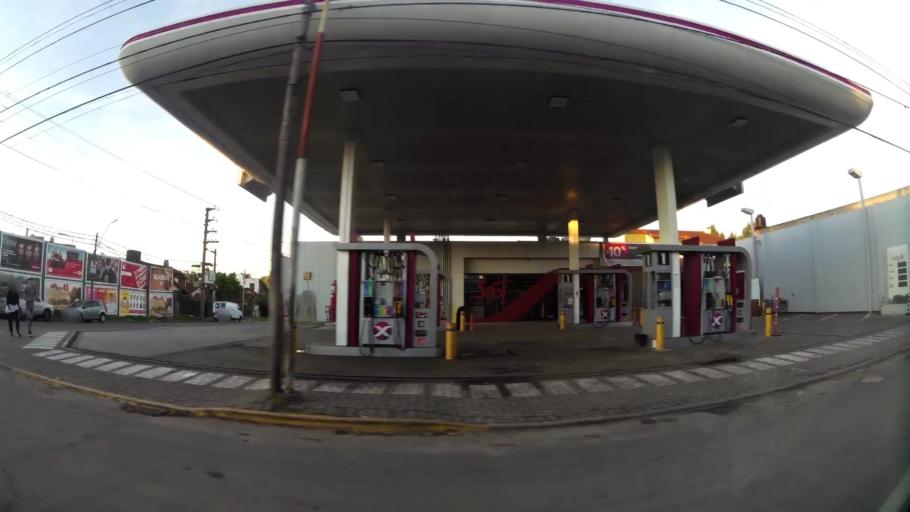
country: AR
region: Buenos Aires
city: Ituzaingo
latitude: -34.6493
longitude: -58.6532
